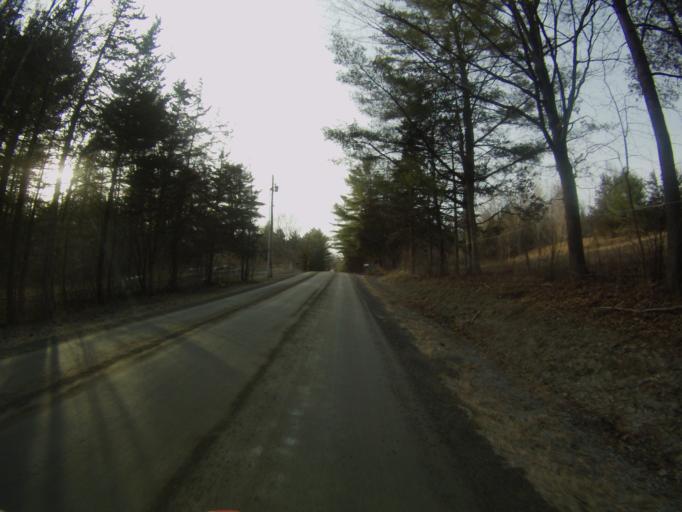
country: US
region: Vermont
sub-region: Addison County
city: Middlebury (village)
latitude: 44.0380
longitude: -73.2754
